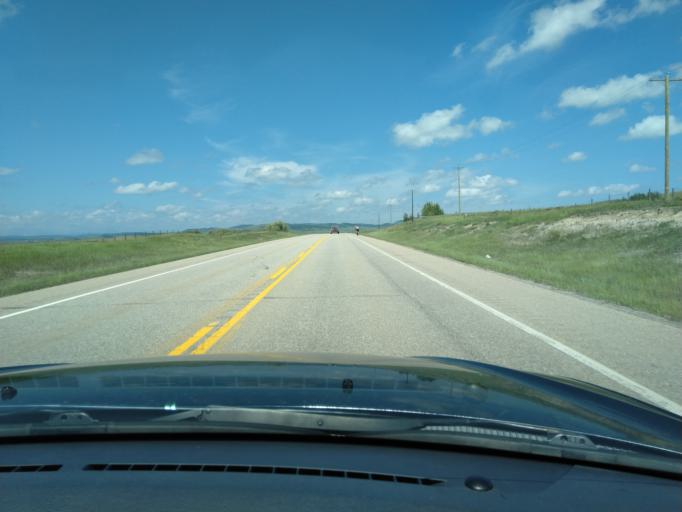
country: CA
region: Alberta
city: Cochrane
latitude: 51.2196
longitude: -114.5421
